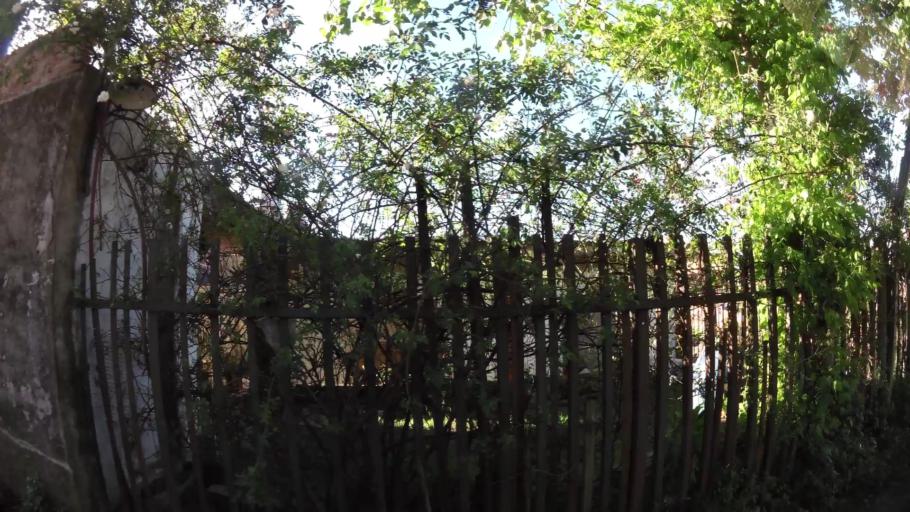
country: AR
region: Buenos Aires
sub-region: Partido de Quilmes
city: Quilmes
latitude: -34.7464
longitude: -58.3167
